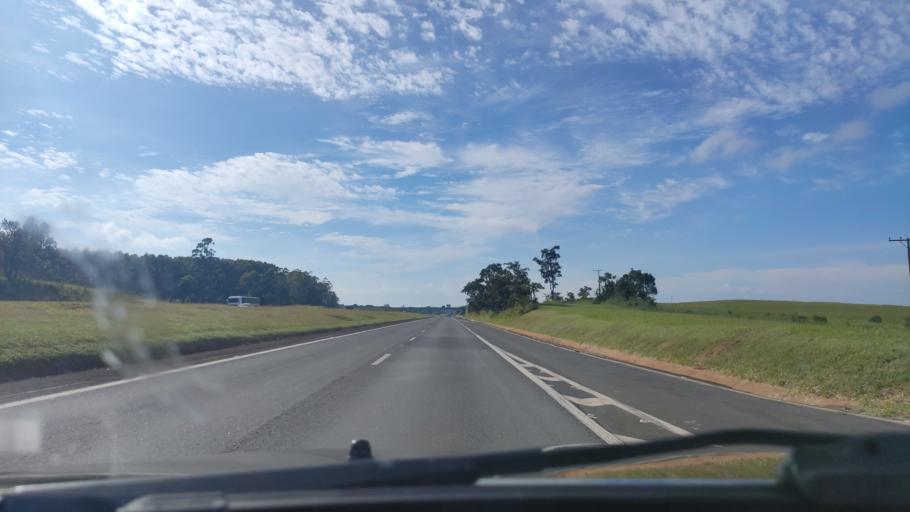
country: BR
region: Sao Paulo
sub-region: Itatinga
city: Itatinga
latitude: -23.0707
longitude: -48.5408
